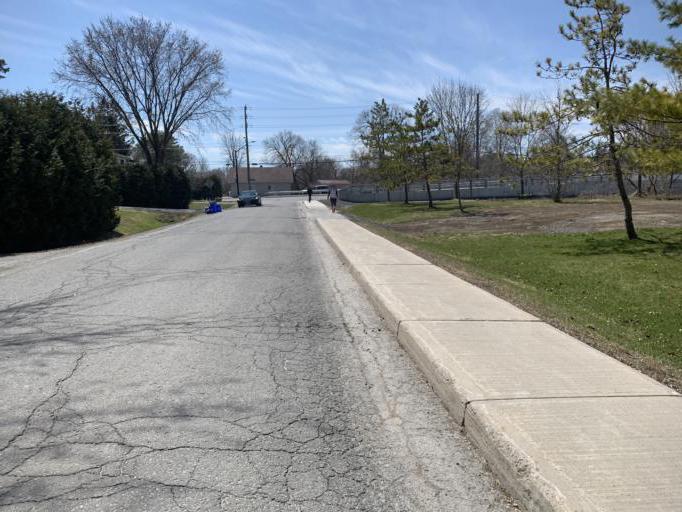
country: CA
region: Ontario
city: Bells Corners
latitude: 45.1893
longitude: -75.8310
